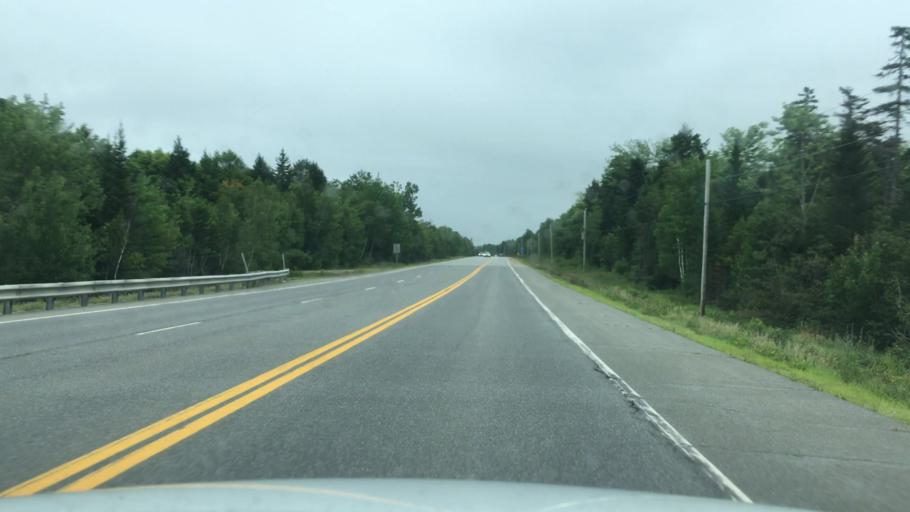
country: US
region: Maine
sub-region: Hancock County
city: Franklin
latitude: 44.8262
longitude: -68.1156
